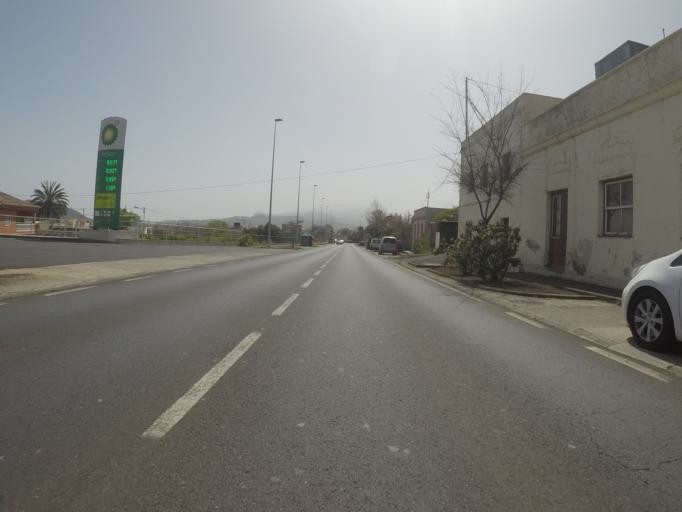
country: ES
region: Canary Islands
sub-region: Provincia de Santa Cruz de Tenerife
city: Tegueste
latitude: 28.5343
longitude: -16.2753
